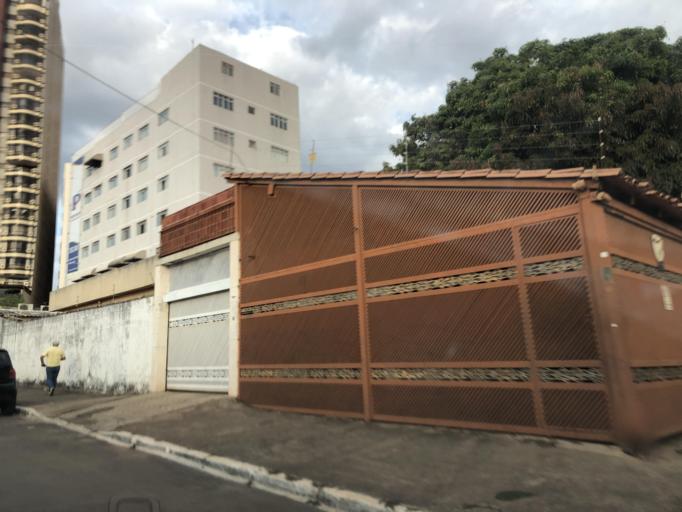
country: BR
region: Federal District
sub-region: Brasilia
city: Brasilia
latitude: -15.8353
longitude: -48.0532
